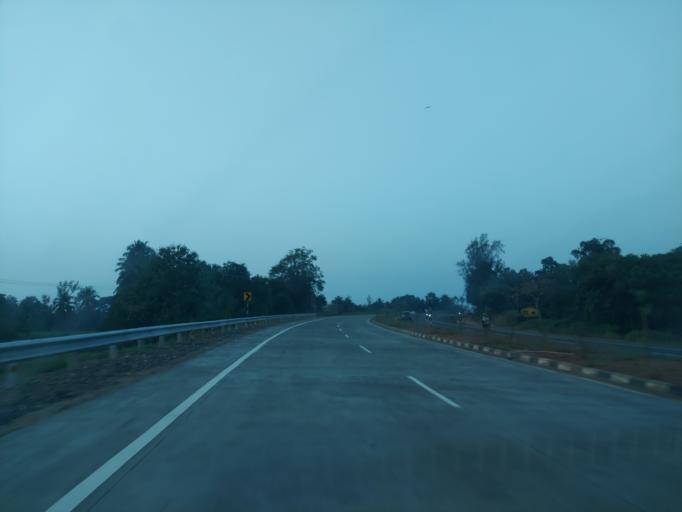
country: IN
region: Maharashtra
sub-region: Sindhudurg
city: Kudal
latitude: 16.0920
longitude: 73.7065
